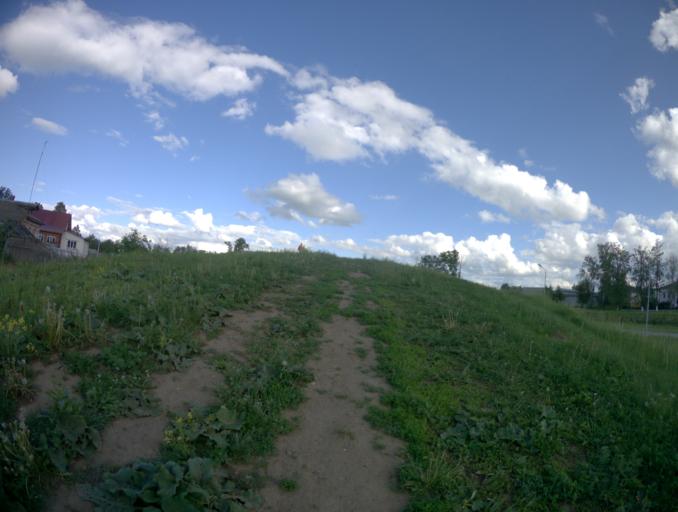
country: RU
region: Vladimir
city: Yur'yev-Pol'skiy
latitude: 56.4960
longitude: 39.6788
